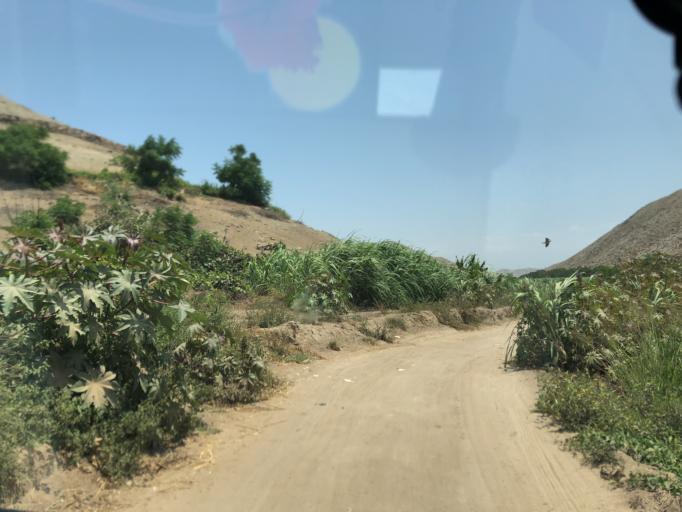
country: PE
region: Lima
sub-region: Provincia de Canete
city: Quilmana
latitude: -12.9908
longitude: -76.4365
